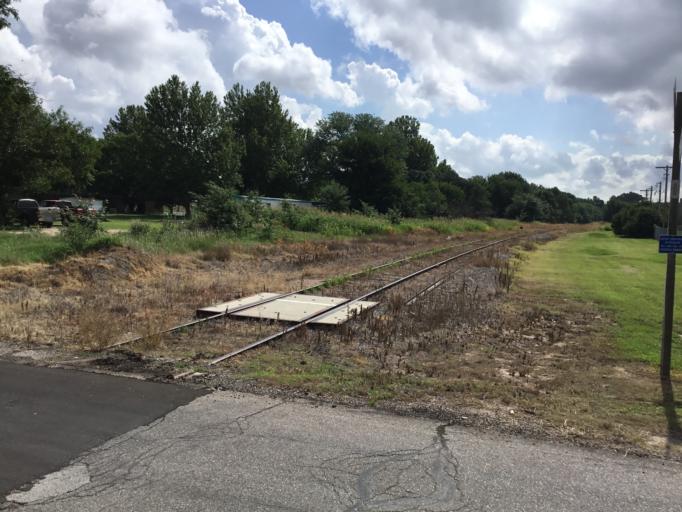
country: US
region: Kansas
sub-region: Pratt County
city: Pratt
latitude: 37.6387
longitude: -98.7213
